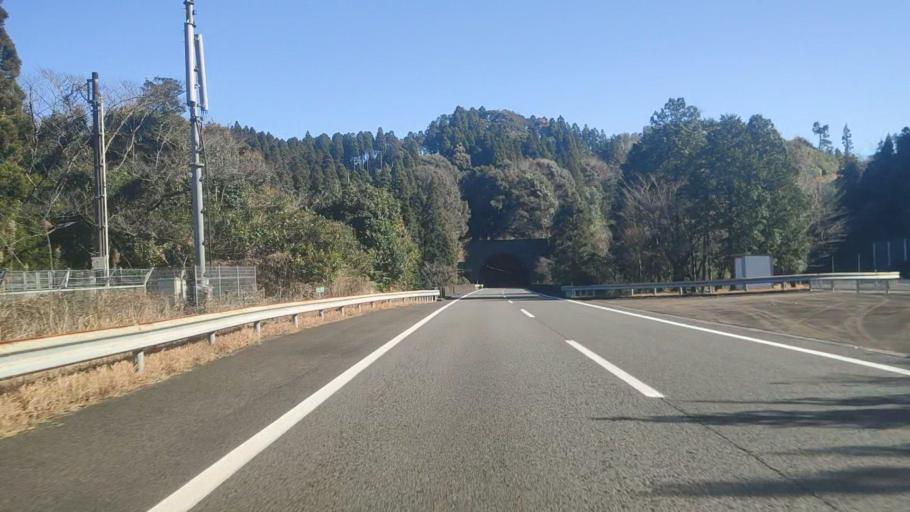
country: JP
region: Miyazaki
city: Miyazaki-shi
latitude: 31.8216
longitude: 131.2547
